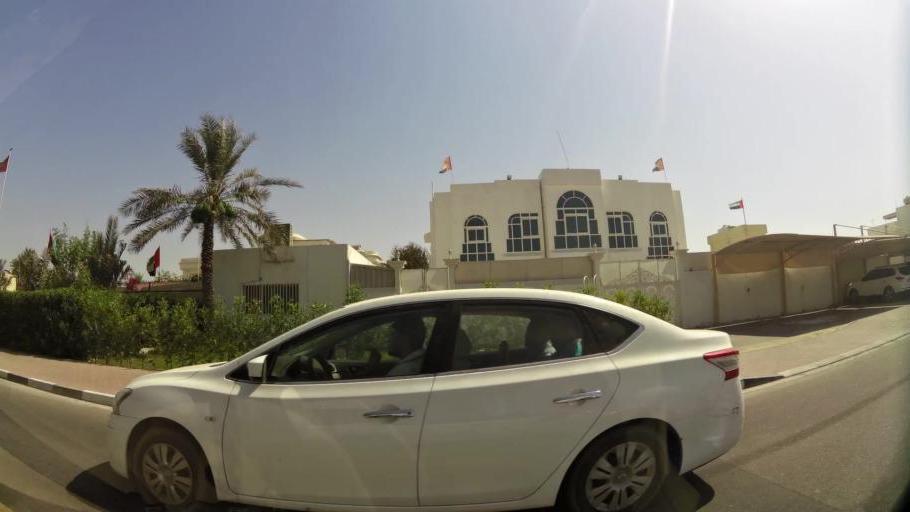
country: AE
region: Ash Shariqah
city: Sharjah
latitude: 25.2681
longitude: 55.3704
